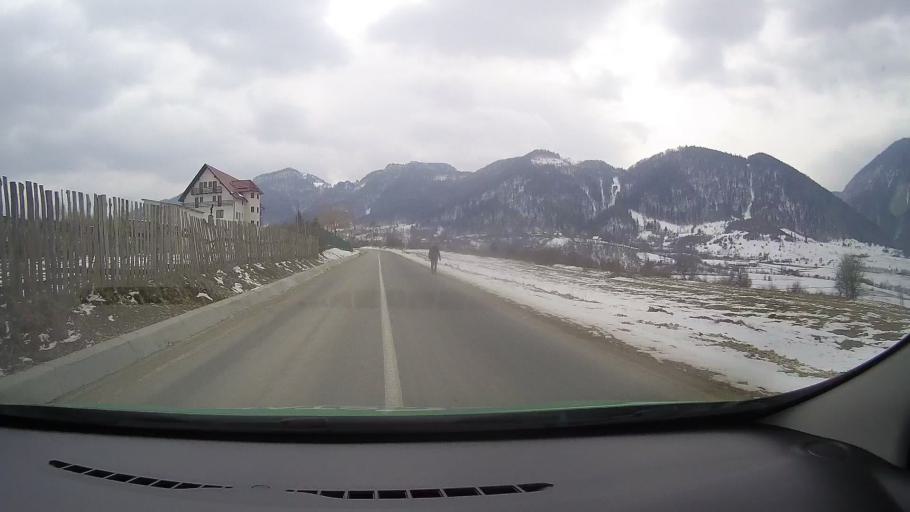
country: RO
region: Brasov
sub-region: Comuna Zarnesti
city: Zarnesti
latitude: 45.5498
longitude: 25.3220
